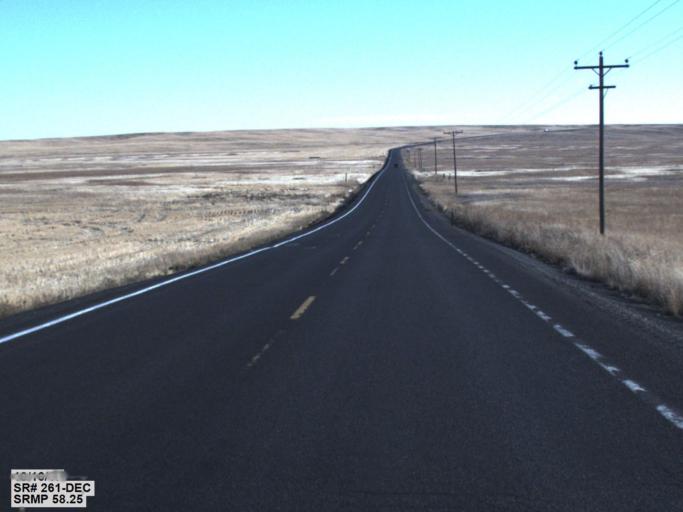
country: US
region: Washington
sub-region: Adams County
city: Ritzville
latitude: 47.0522
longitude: -118.3581
